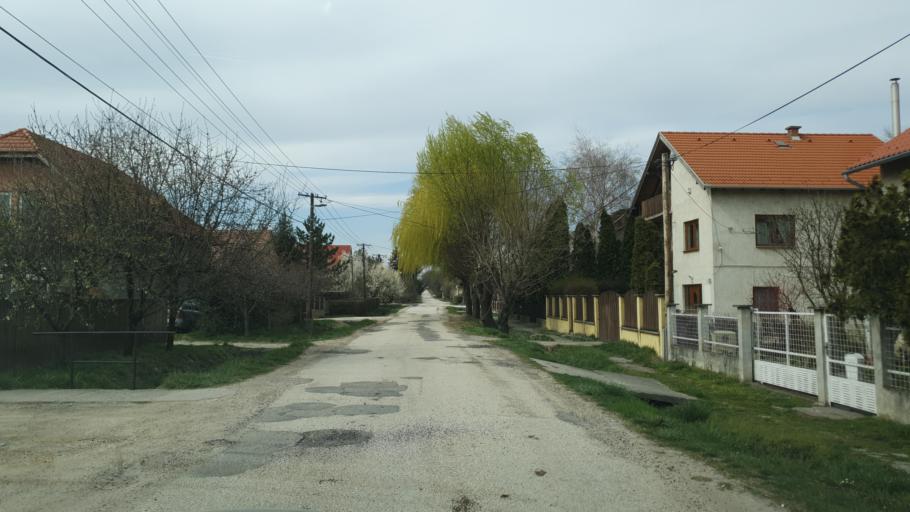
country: HU
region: Fejer
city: Etyek
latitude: 47.4494
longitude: 18.7560
